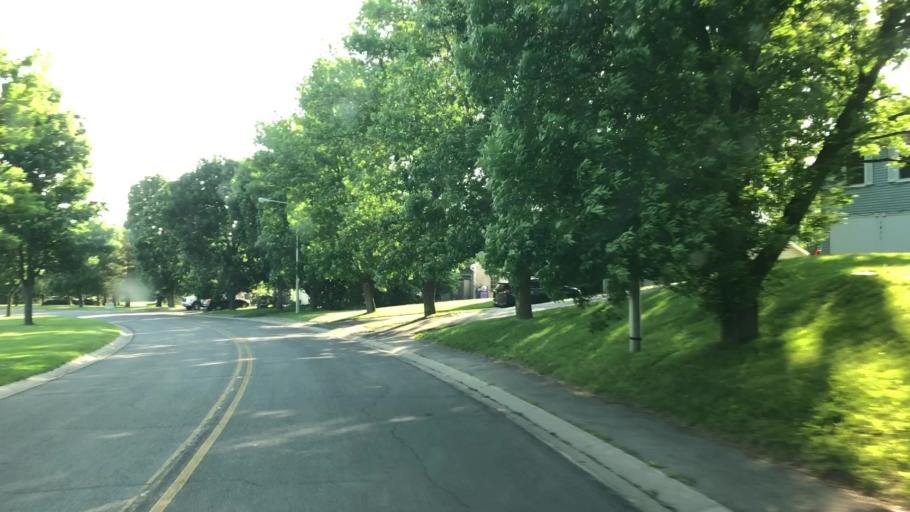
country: US
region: New York
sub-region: Wayne County
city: Macedon
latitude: 43.1221
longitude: -77.3109
